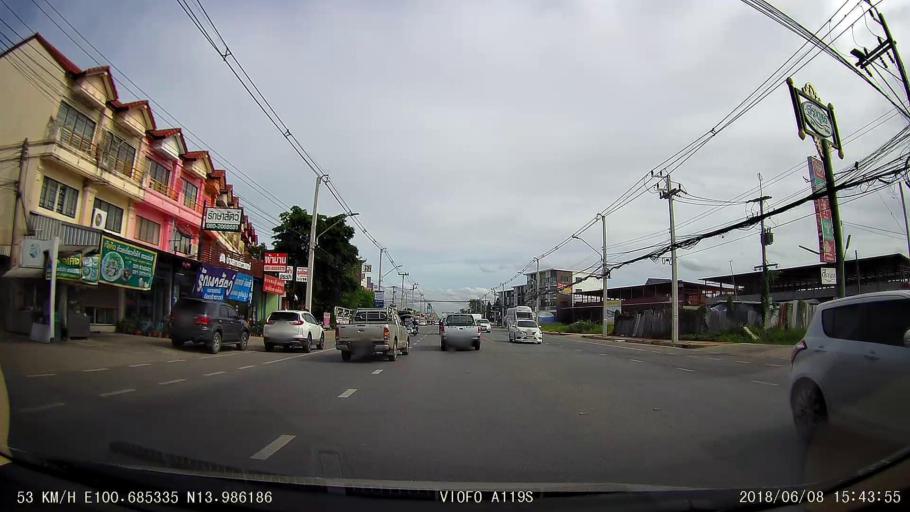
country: TH
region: Pathum Thani
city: Thanyaburi
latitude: 13.9860
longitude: 100.6853
